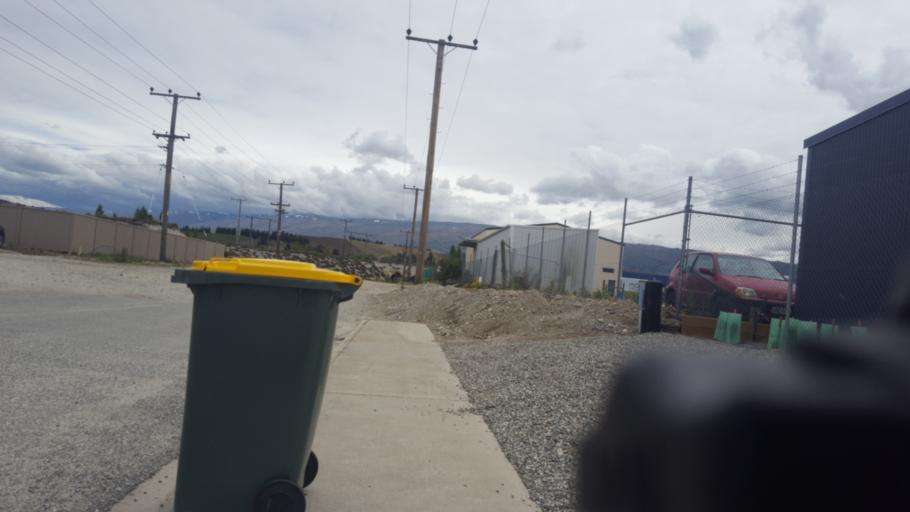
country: NZ
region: Otago
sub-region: Queenstown-Lakes District
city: Wanaka
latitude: -45.2493
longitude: 169.3728
